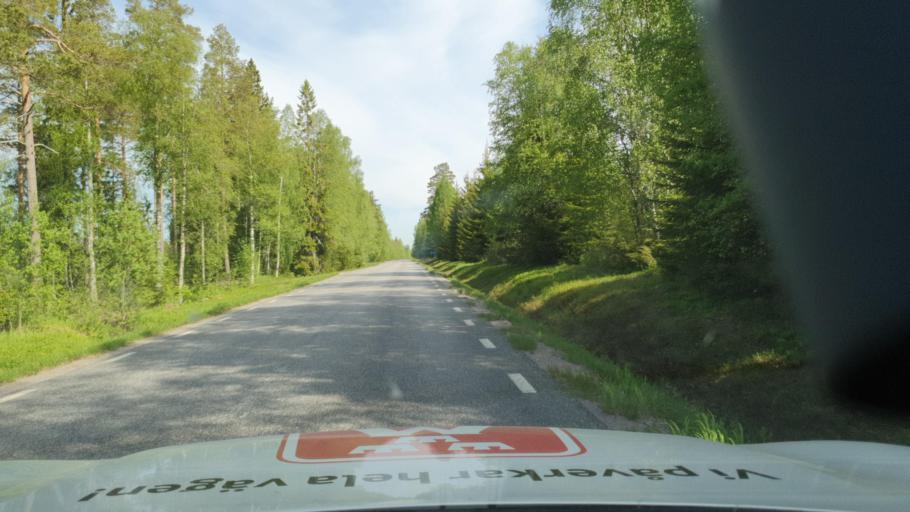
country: SE
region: Vaesterbotten
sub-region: Vannas Kommun
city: Vannasby
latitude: 63.8178
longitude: 19.8563
